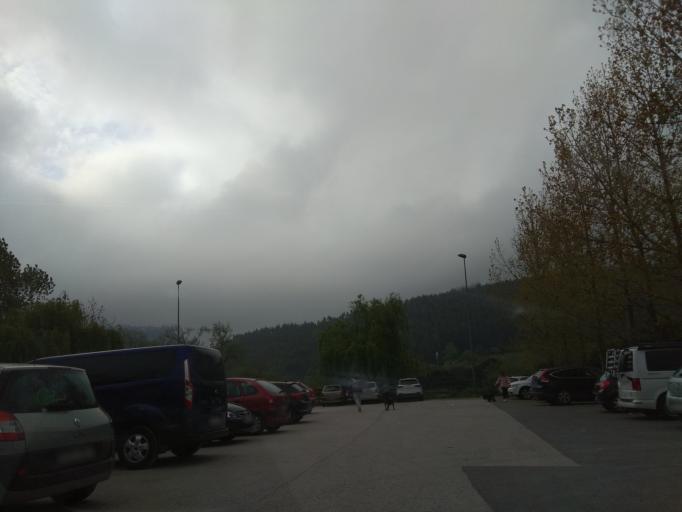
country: ES
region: Cantabria
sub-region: Provincia de Cantabria
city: San Vicente de la Barquera
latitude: 43.3739
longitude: -4.4628
